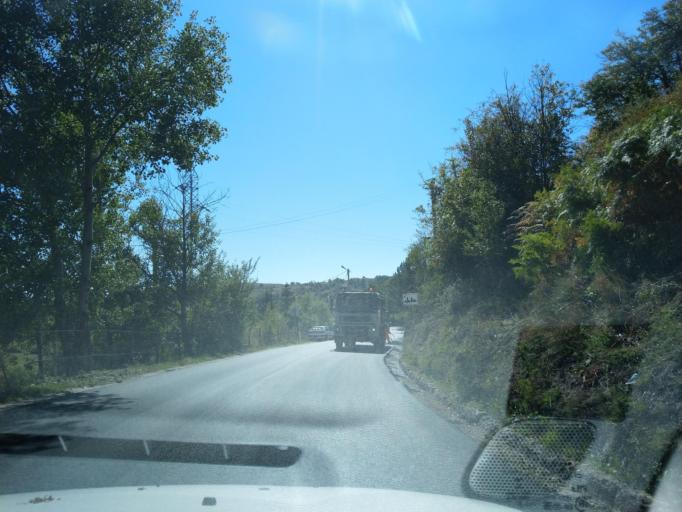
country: RS
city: Sokolovica
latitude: 43.2555
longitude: 20.2300
